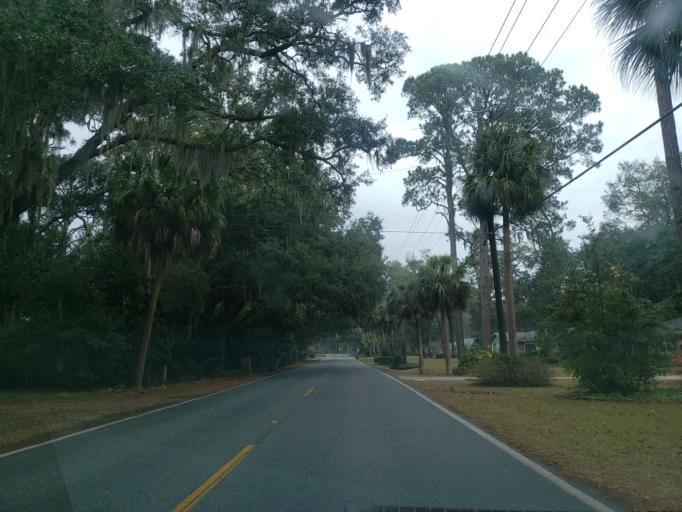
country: US
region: Georgia
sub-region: Chatham County
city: Wilmington Island
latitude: 31.9958
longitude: -80.9952
